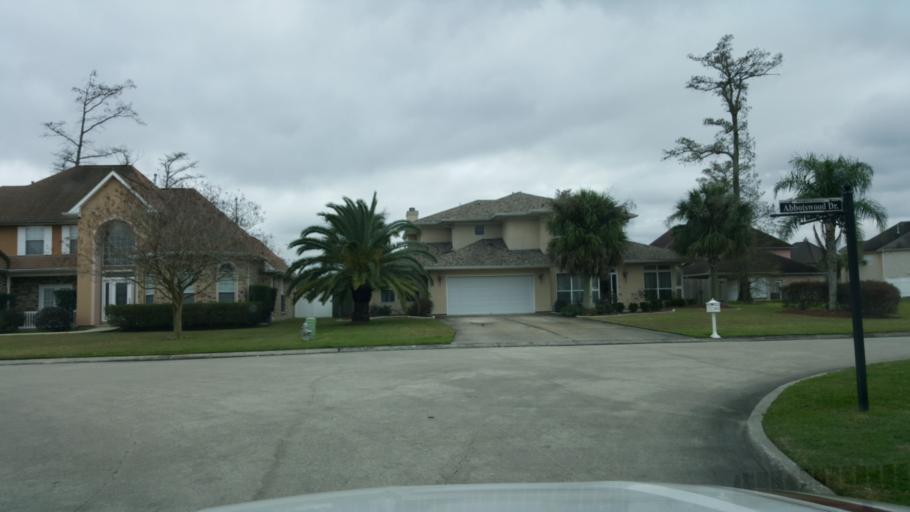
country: US
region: Louisiana
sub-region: Jefferson Parish
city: Harvey
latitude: 29.8811
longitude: -90.0793
